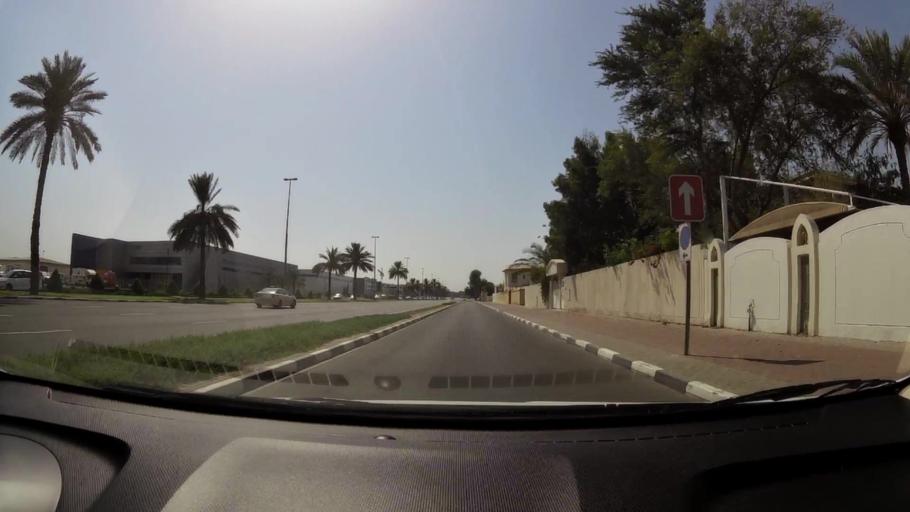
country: AE
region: Ash Shariqah
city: Sharjah
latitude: 25.2645
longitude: 55.3703
